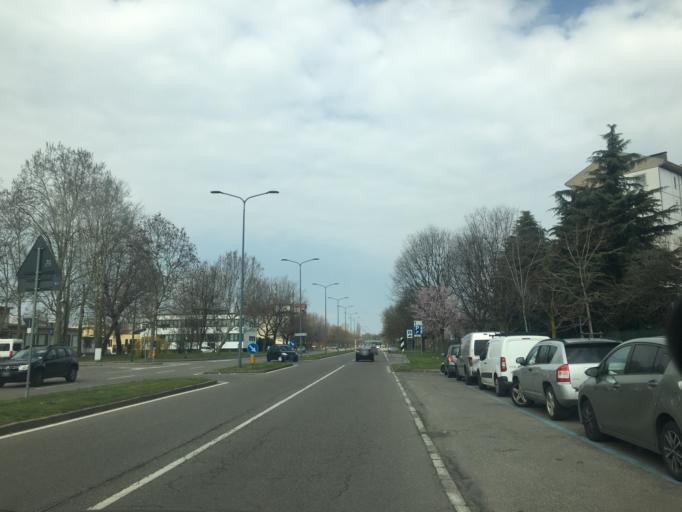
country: IT
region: Lombardy
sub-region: Citta metropolitana di Milano
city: Bresso
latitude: 45.5220
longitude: 9.2051
